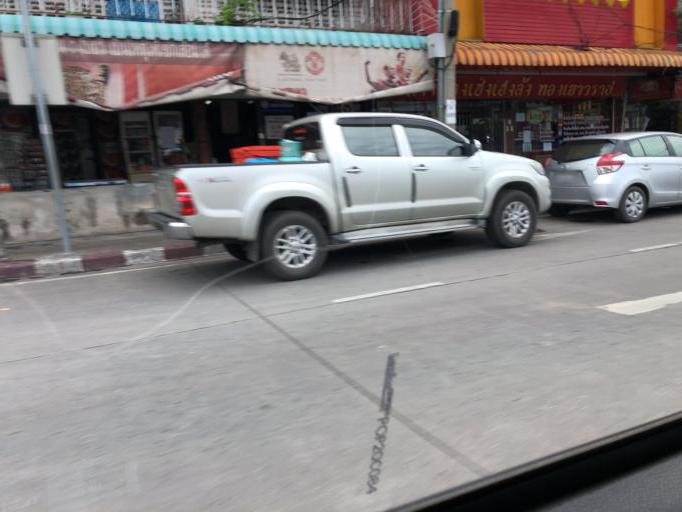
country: TH
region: Bangkok
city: Don Mueang
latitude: 13.9244
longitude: 100.5966
